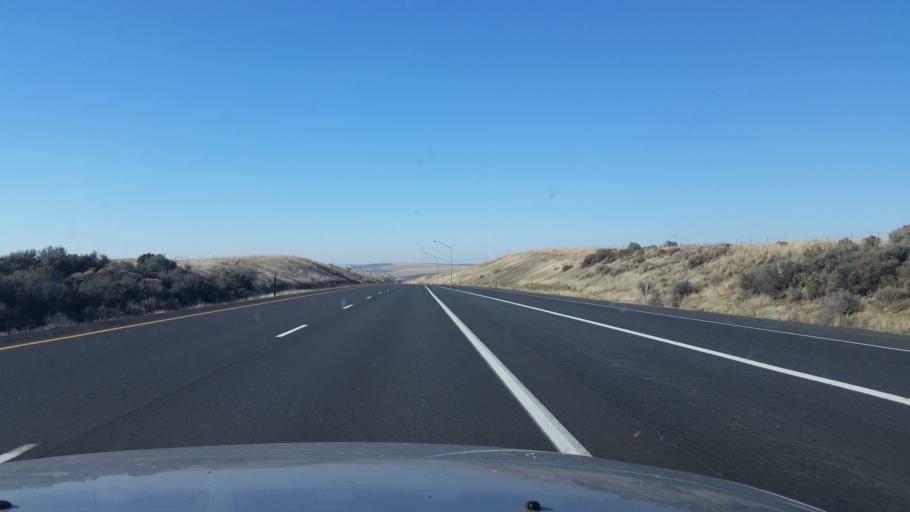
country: US
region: Washington
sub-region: Grant County
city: Warden
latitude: 47.0868
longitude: -118.8526
